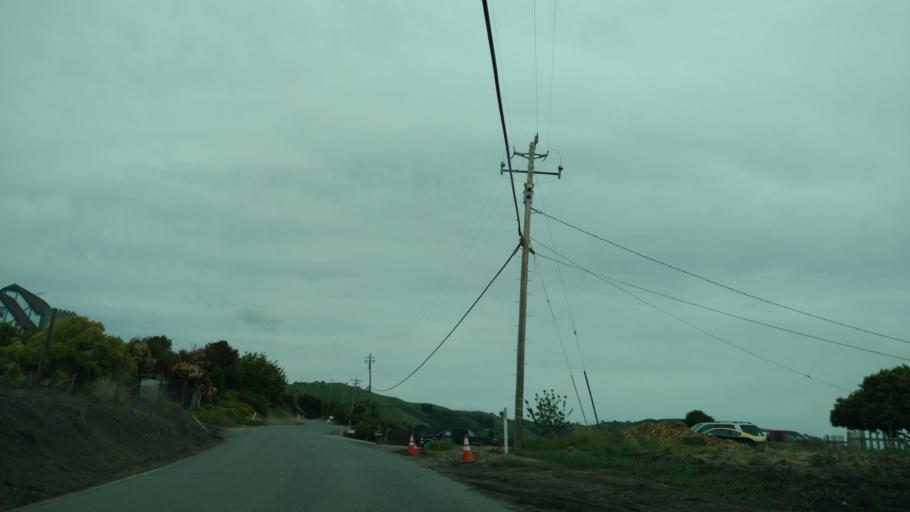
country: US
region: California
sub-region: Santa Clara County
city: East Foothills
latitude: 37.3759
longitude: -121.7961
